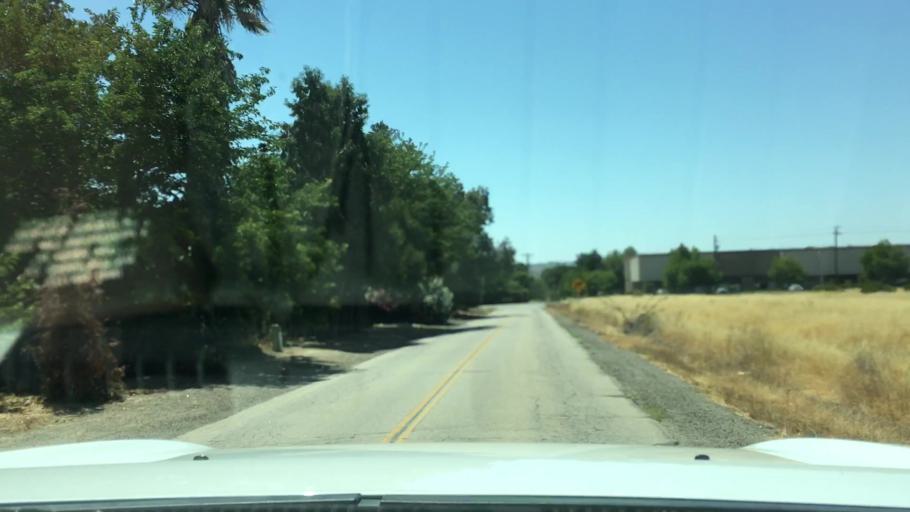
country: US
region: California
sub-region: San Luis Obispo County
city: Paso Robles
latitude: 35.6119
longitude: -120.6425
